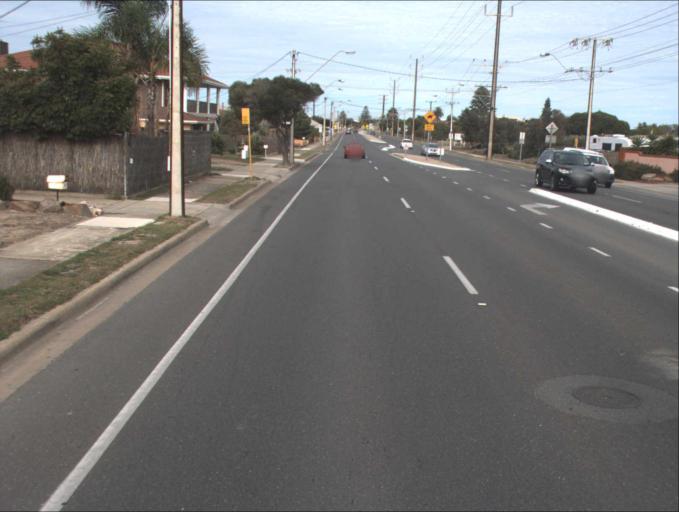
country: AU
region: South Australia
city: Port Adelaide
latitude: -34.8522
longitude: 138.4790
